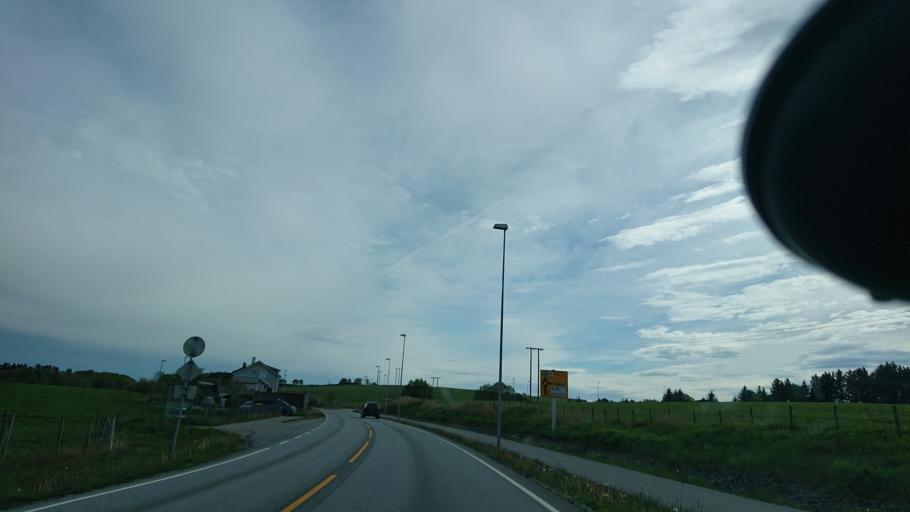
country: NO
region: Rogaland
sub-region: Sola
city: Tananger
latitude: 58.9461
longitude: 5.5991
